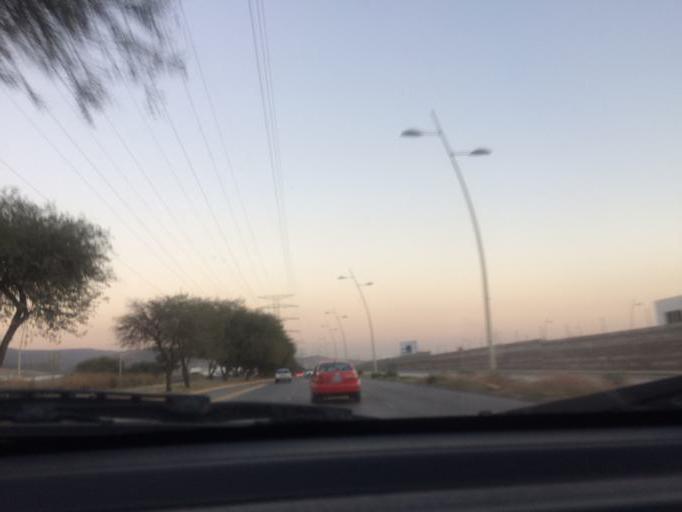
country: MX
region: Guanajuato
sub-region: Leon
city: Medina
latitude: 21.1357
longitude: -101.6174
